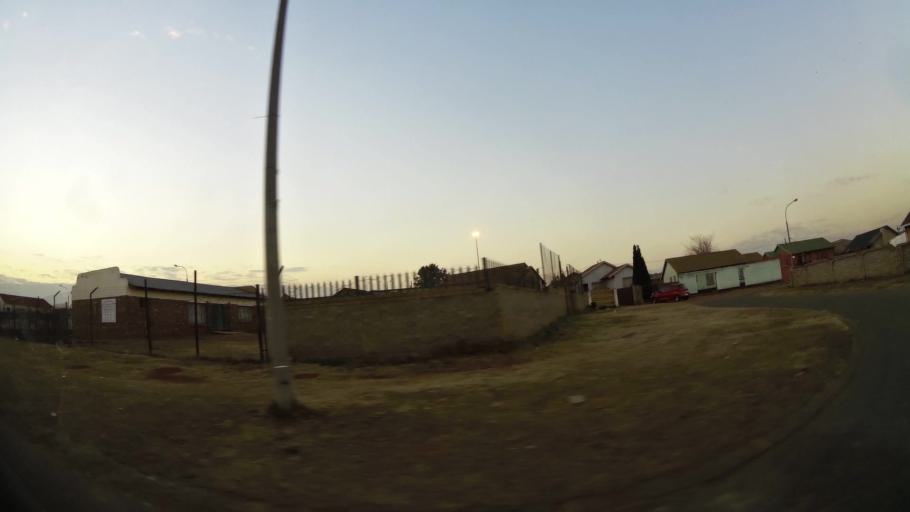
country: ZA
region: Gauteng
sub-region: West Rand District Municipality
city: Randfontein
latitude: -26.2120
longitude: 27.7170
